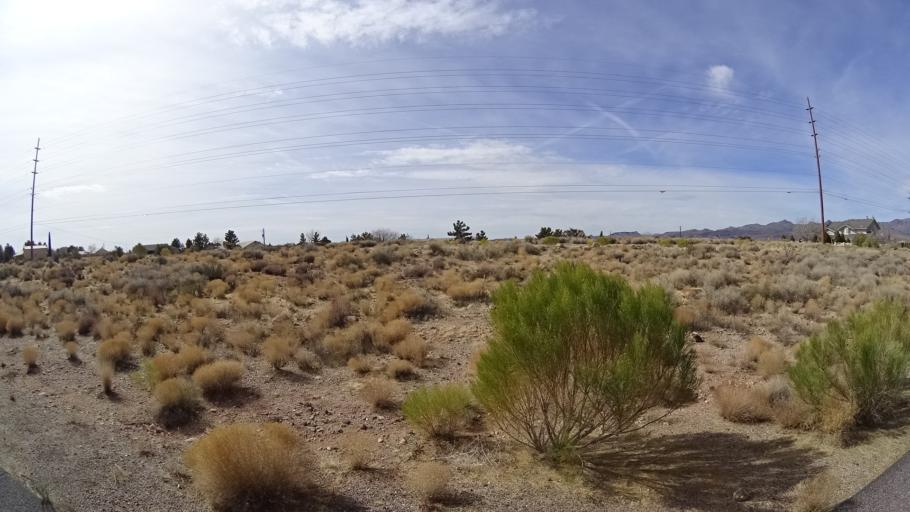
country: US
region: Arizona
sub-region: Mohave County
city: Kingman
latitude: 35.1876
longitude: -113.9842
